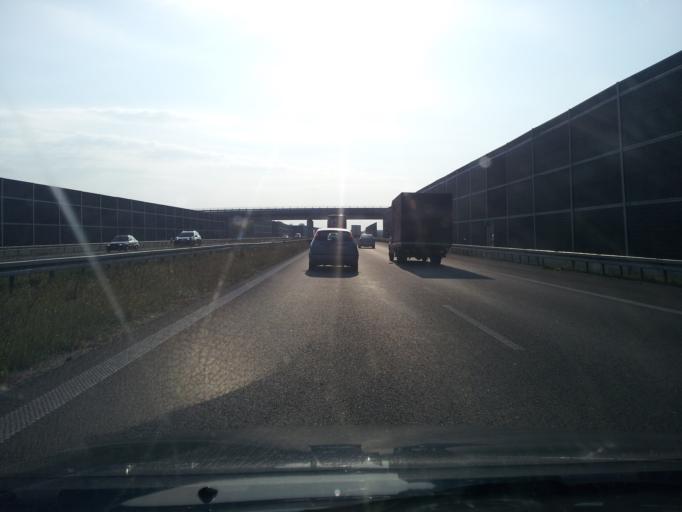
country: PL
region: Masovian Voivodeship
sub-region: Powiat zyrardowski
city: Guzow
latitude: 52.0764
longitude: 20.3274
